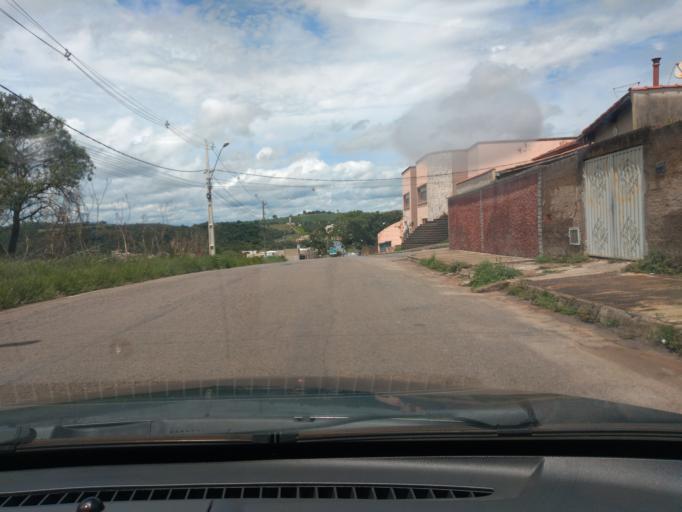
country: BR
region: Minas Gerais
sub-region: Tres Coracoes
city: Tres Coracoes
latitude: -21.6782
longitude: -45.2703
